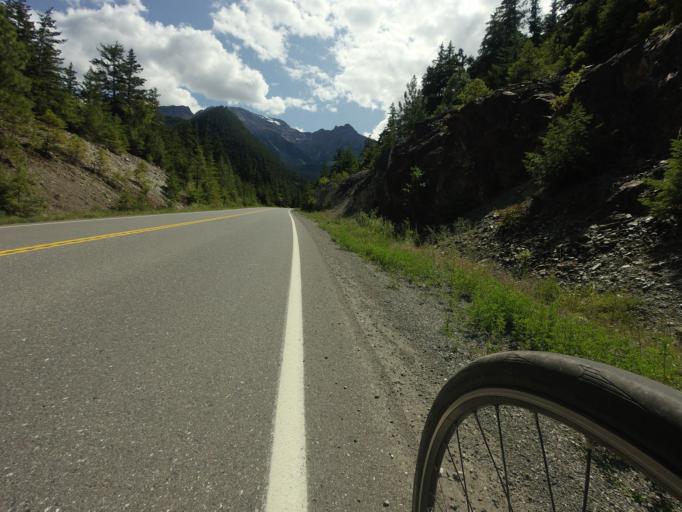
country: CA
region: British Columbia
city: Lillooet
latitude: 50.6611
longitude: -121.9919
